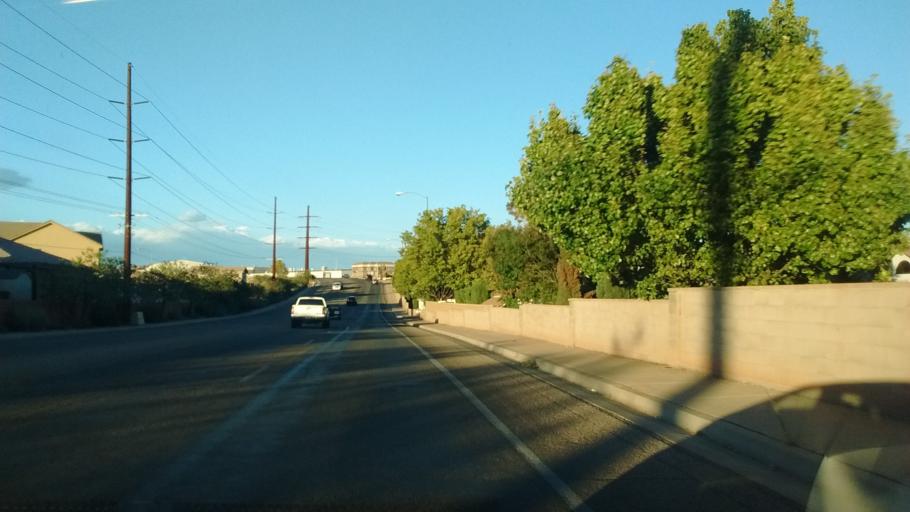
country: US
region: Utah
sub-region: Washington County
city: Washington
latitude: 37.1093
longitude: -113.5232
